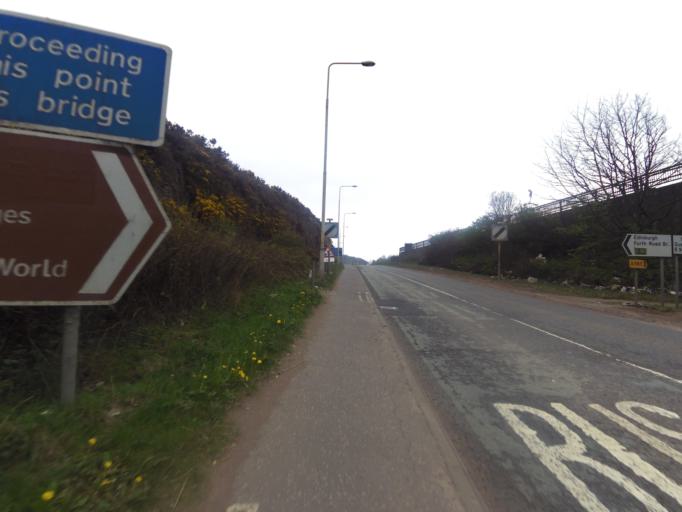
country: GB
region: Scotland
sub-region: Fife
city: Inverkeithing
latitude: 56.0207
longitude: -3.4058
